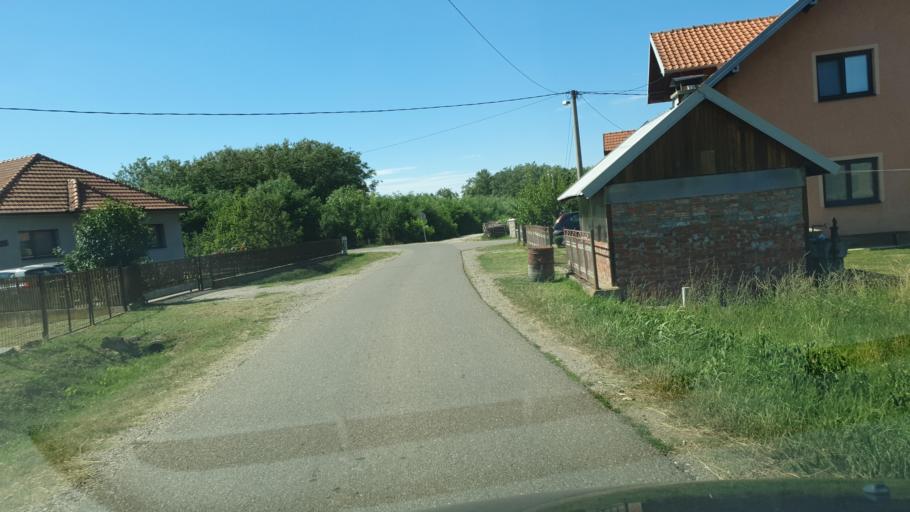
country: BA
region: Republika Srpska
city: Bijeljina
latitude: 44.7253
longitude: 19.2038
